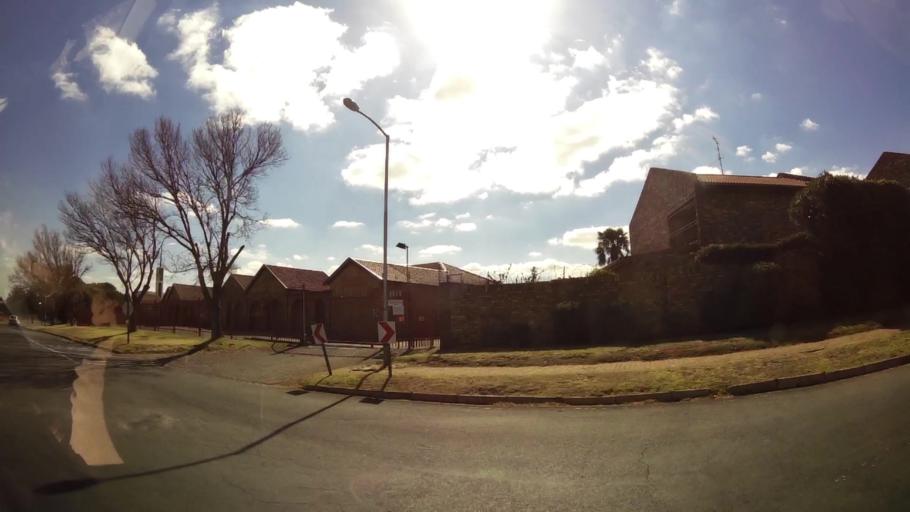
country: ZA
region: Gauteng
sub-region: West Rand District Municipality
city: Krugersdorp
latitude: -26.1017
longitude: 27.7943
